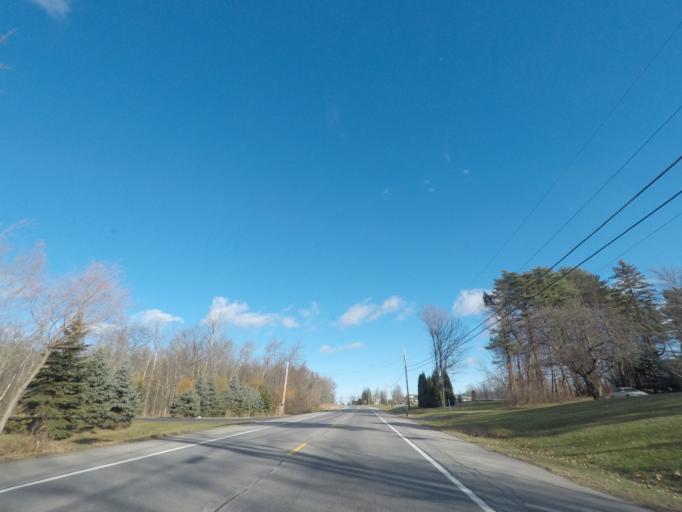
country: US
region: New York
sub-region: Saratoga County
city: Mechanicville
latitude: 42.8504
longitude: -73.7291
